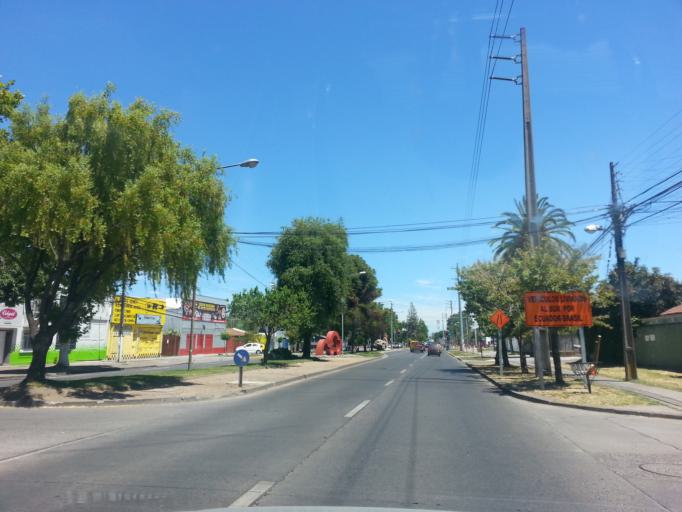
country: CL
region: Biobio
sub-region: Provincia de Nuble
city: Chillan
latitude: -36.5988
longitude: -72.1043
